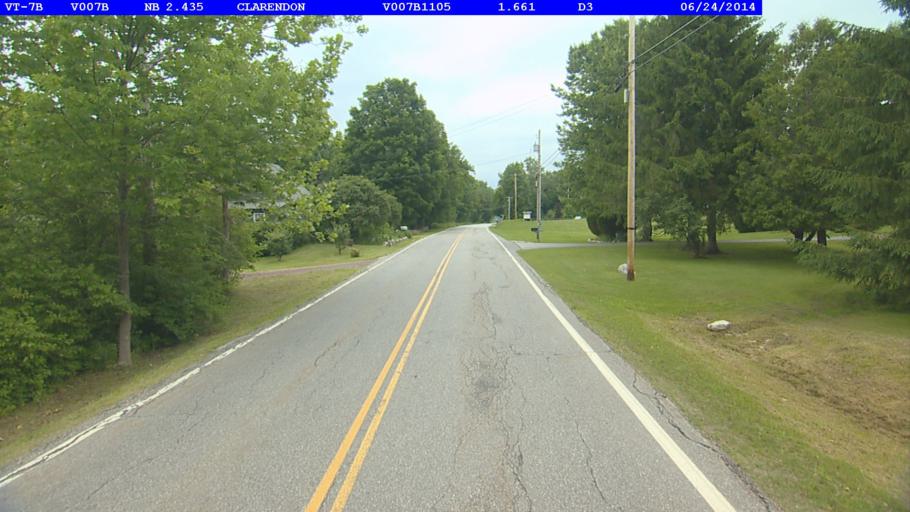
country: US
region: Vermont
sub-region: Rutland County
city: Rutland
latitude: 43.5248
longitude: -72.9598
